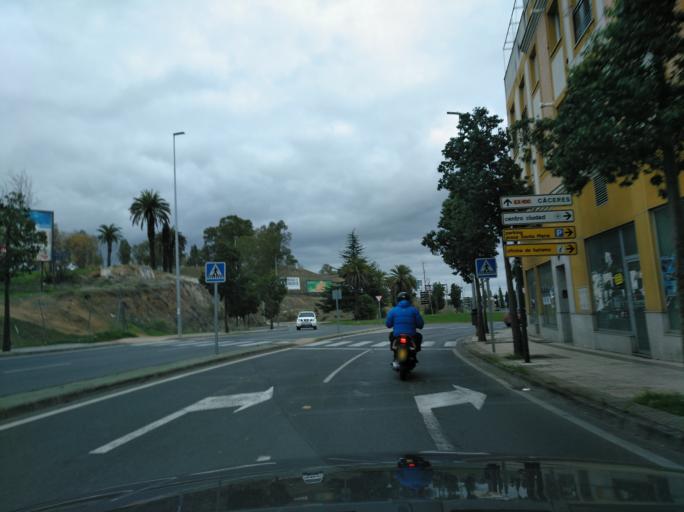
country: ES
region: Extremadura
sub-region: Provincia de Badajoz
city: Badajoz
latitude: 38.8863
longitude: -6.9763
